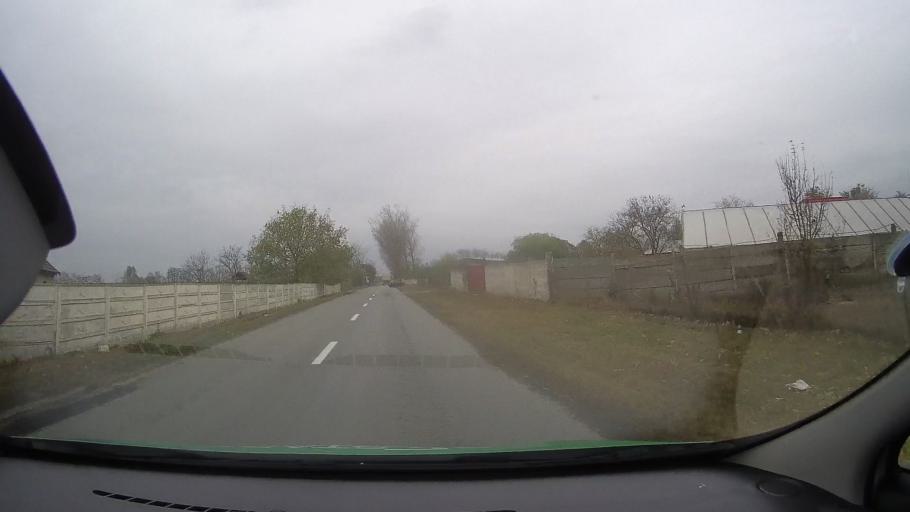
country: RO
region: Constanta
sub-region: Comuna Mihail Kogalniceanu
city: Mihail Kogalniceanu
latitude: 44.3796
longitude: 28.4645
